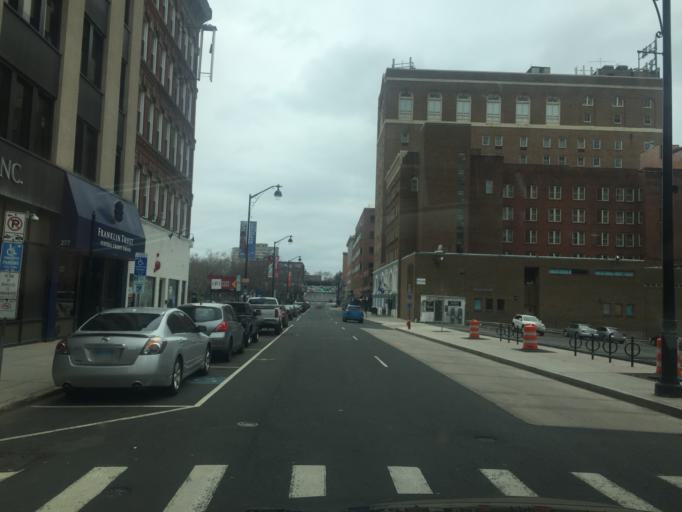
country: US
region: Connecticut
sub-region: Hartford County
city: Hartford
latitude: 41.7674
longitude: -72.6779
